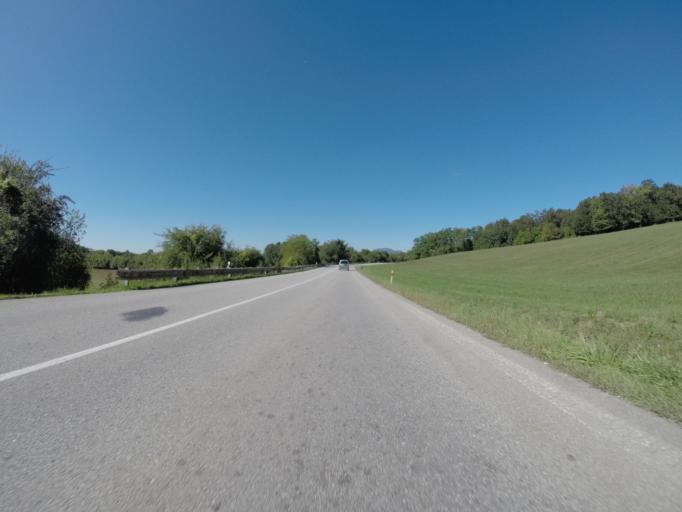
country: SK
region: Nitriansky
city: Puchov
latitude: 49.0688
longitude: 18.3472
